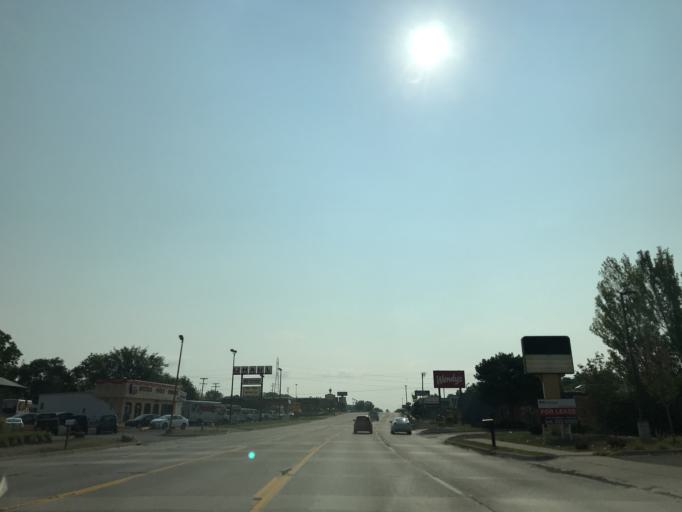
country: US
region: Michigan
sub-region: Washtenaw County
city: Ypsilanti
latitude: 42.2497
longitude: -83.6556
